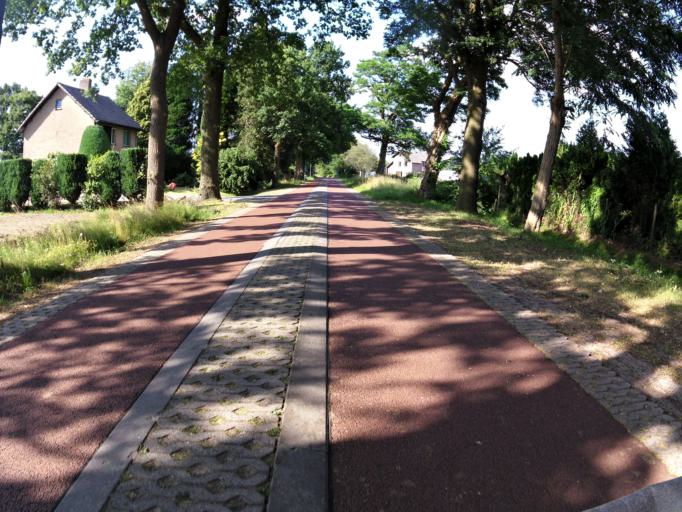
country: NL
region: North Brabant
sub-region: Gemeente Vught
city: Vught
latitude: 51.6267
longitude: 5.2768
